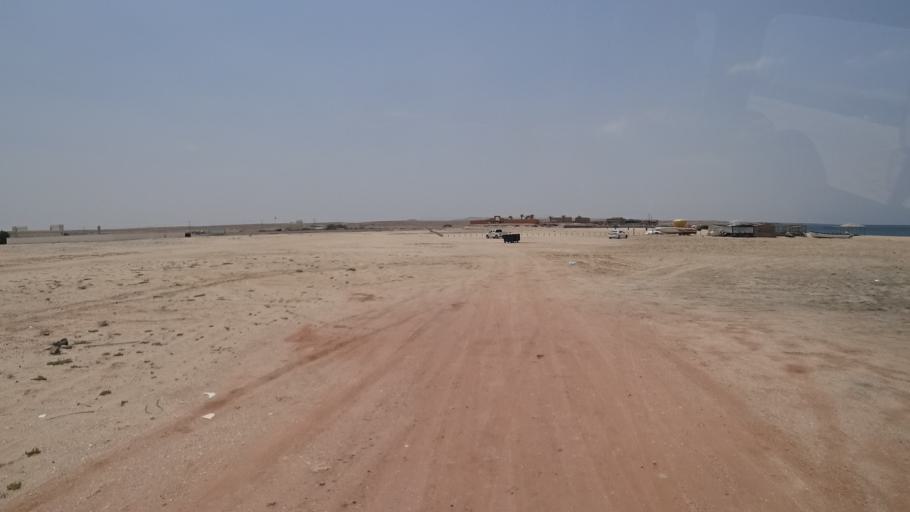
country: OM
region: Ash Sharqiyah
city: Sur
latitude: 22.5325
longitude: 59.7664
